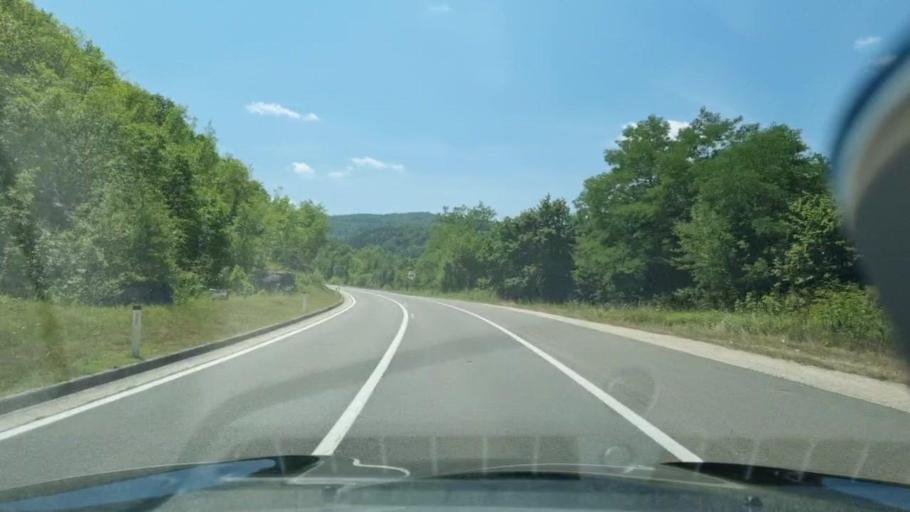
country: BA
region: Federation of Bosnia and Herzegovina
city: Velagici
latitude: 44.5554
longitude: 16.7066
